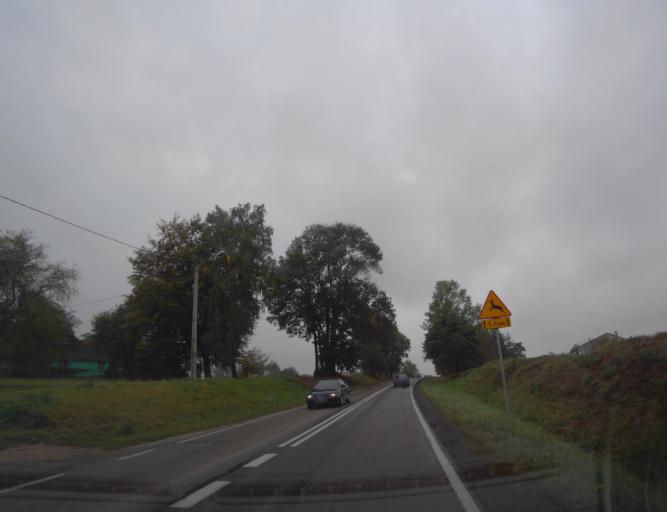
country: PL
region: Lublin Voivodeship
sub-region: Powiat krasnostawski
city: Krasnystaw
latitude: 51.0272
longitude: 23.2207
